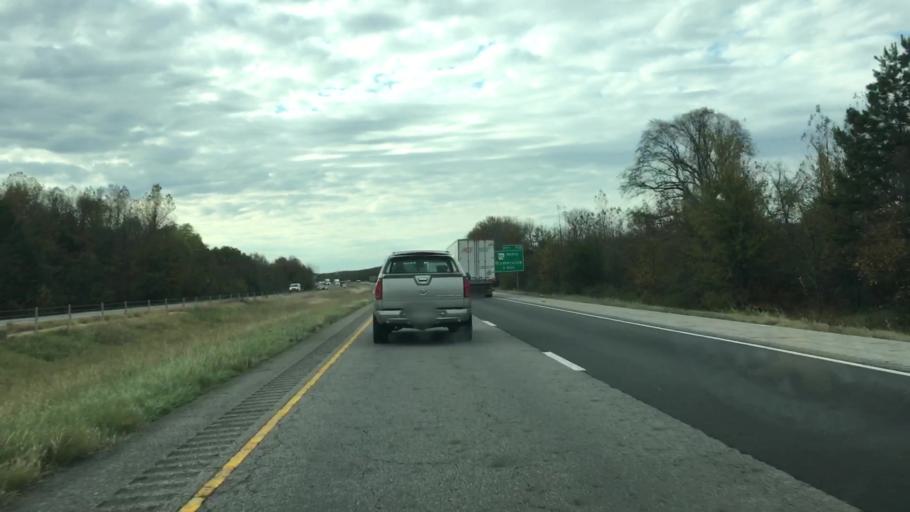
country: US
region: Arkansas
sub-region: Conway County
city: Morrilton
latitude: 35.1630
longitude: -92.6182
